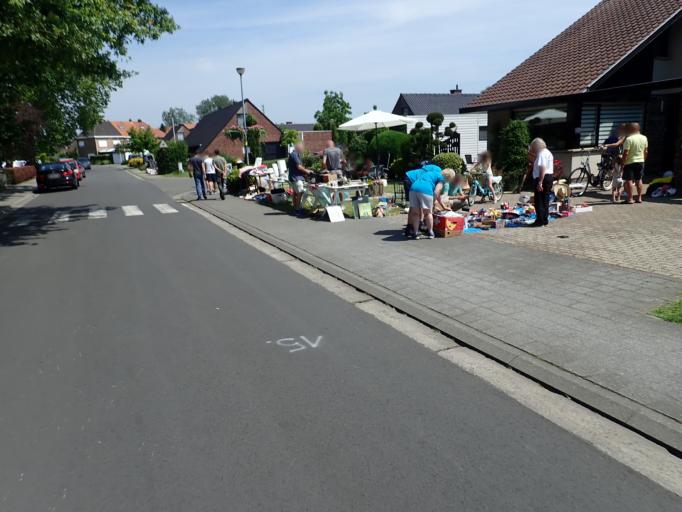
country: BE
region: Flanders
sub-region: Provincie Oost-Vlaanderen
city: Hamme
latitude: 51.0921
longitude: 4.1247
